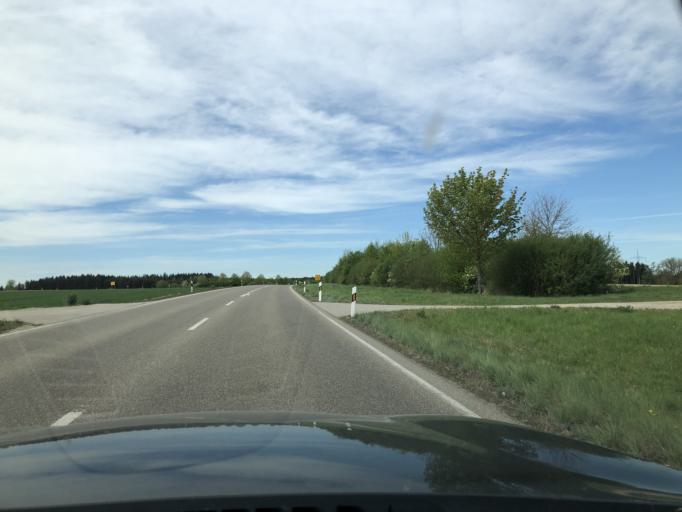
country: DE
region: Bavaria
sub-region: Swabia
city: Biberbach
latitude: 48.5229
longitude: 10.7964
